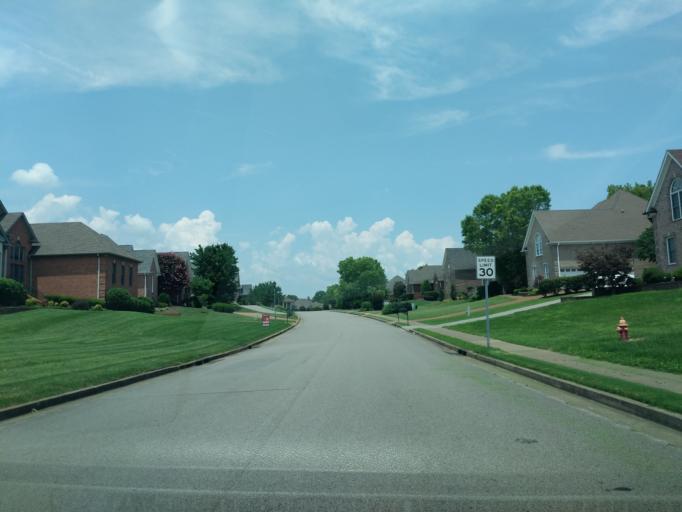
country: US
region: Tennessee
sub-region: Davidson County
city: Lakewood
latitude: 36.2307
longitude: -86.6301
